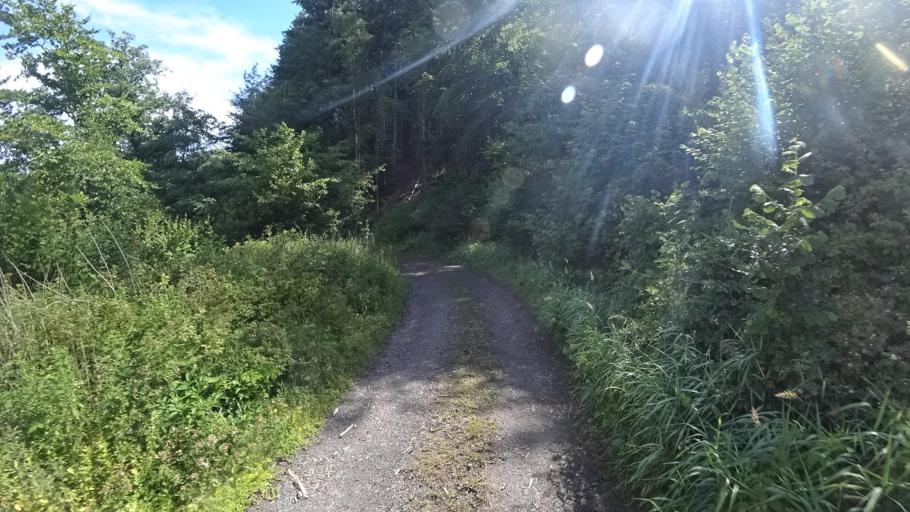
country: DE
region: Rheinland-Pfalz
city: Schoneberg
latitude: 50.6628
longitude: 7.5962
